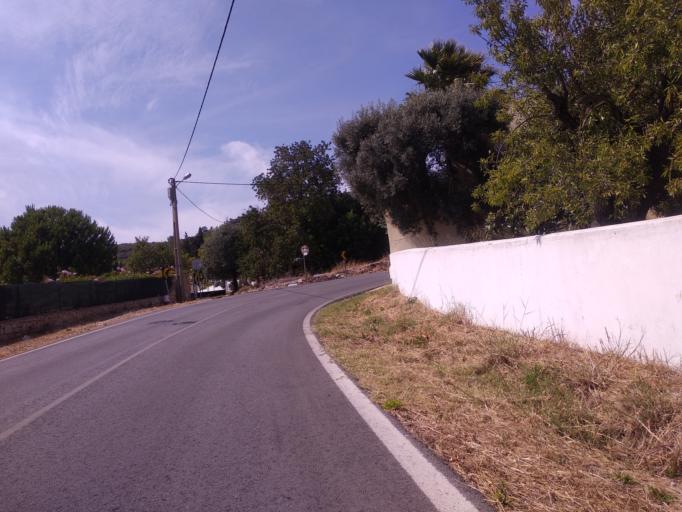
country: PT
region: Faro
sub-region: Faro
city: Santa Barbara de Nexe
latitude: 37.1123
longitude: -7.9623
